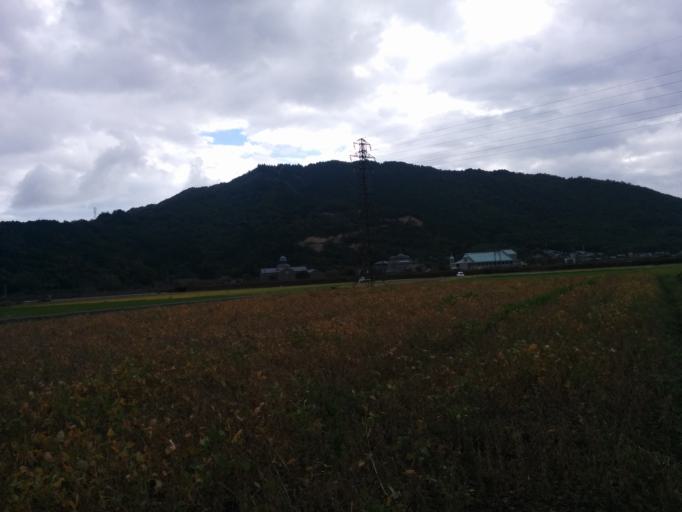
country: JP
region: Shiga Prefecture
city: Omihachiman
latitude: 35.1508
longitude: 136.1397
